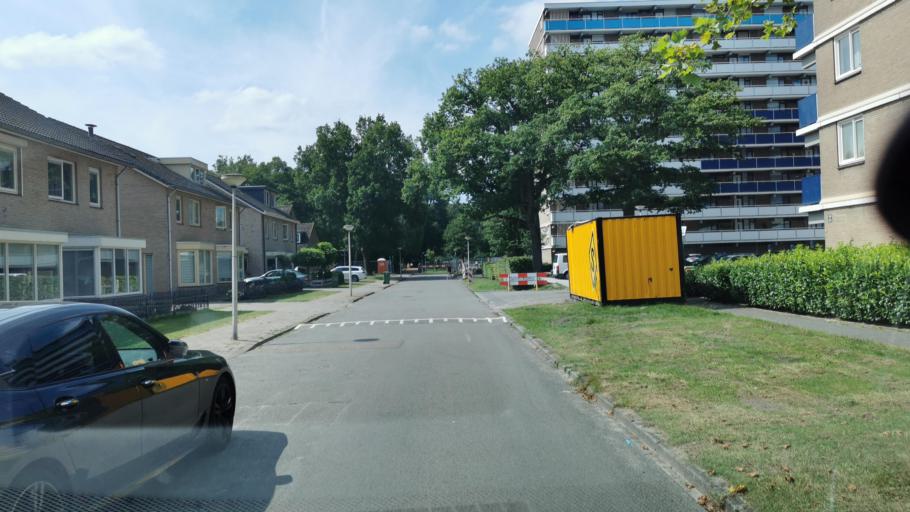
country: NL
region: Overijssel
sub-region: Gemeente Enschede
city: Enschede
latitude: 52.1896
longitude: 6.8798
